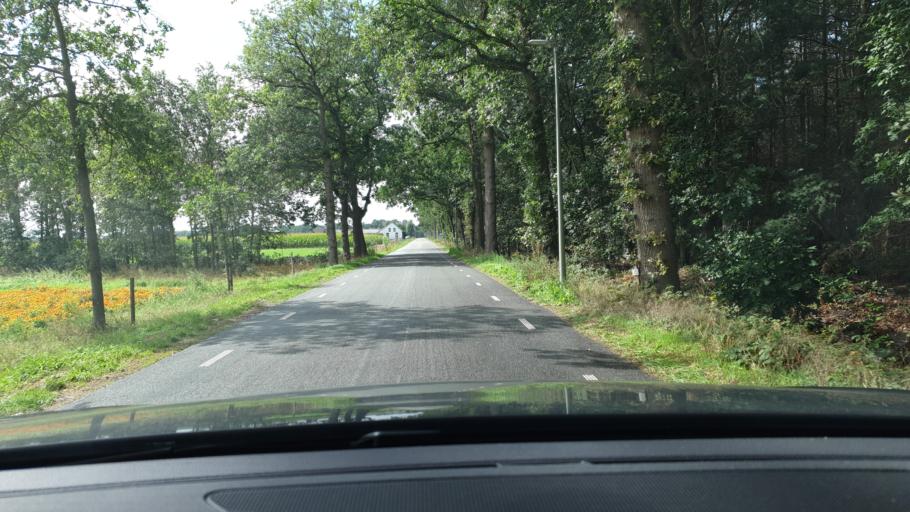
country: NL
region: Limburg
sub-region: Gemeente Venray
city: Venray
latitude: 51.5436
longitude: 6.0372
